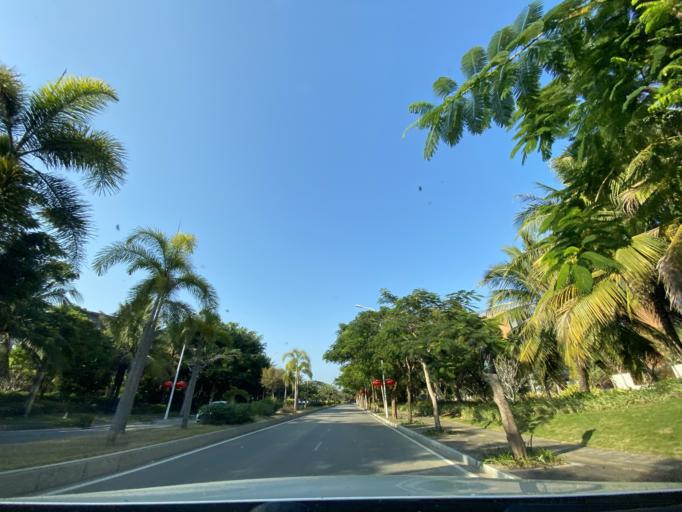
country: CN
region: Hainan
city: Haitangwan
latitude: 18.4079
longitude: 109.7813
